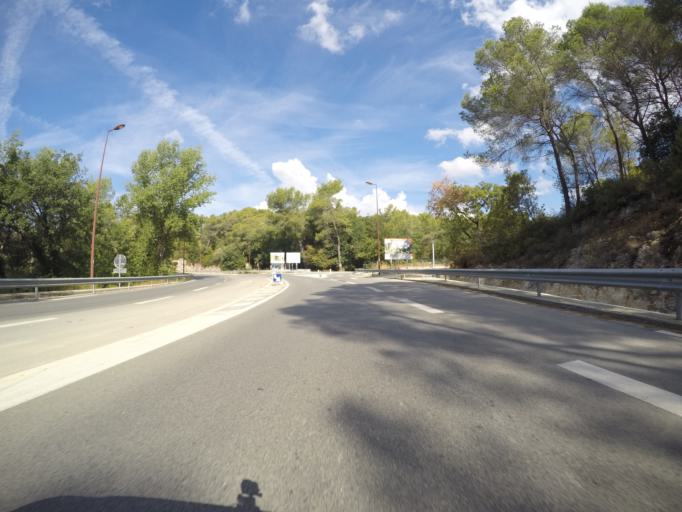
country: FR
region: Provence-Alpes-Cote d'Azur
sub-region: Departement des Alpes-Maritimes
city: Le Rouret
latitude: 43.6720
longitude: 7.0281
